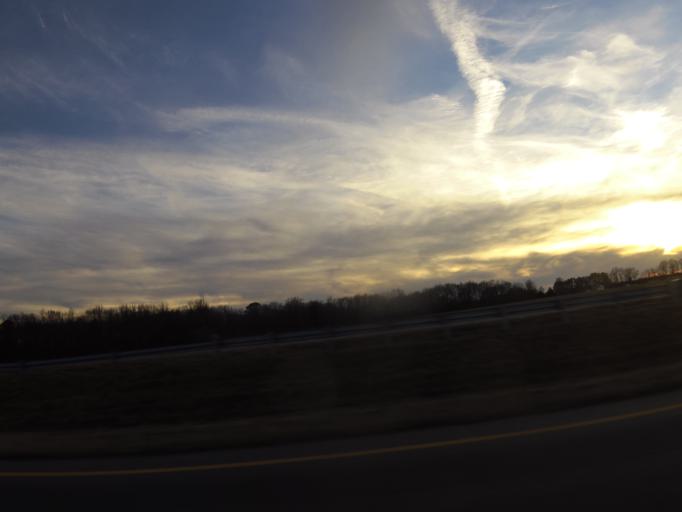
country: US
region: Virginia
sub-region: City of Franklin
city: Franklin
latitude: 36.6859
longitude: -76.9720
